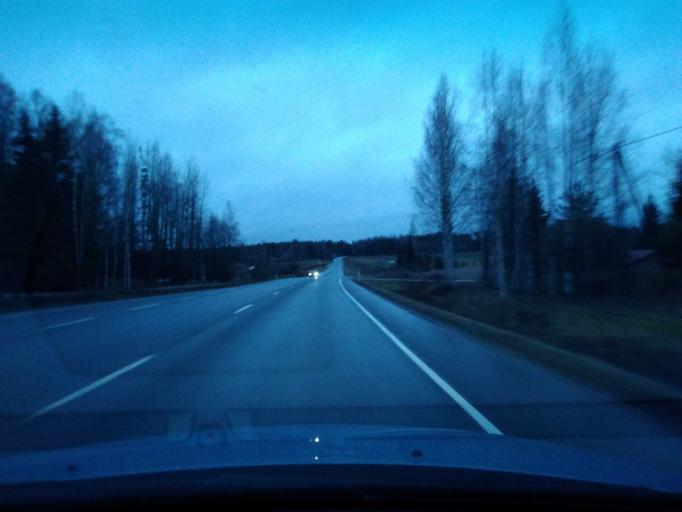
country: FI
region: Uusimaa
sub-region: Porvoo
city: Porvoo
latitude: 60.4114
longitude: 25.5823
